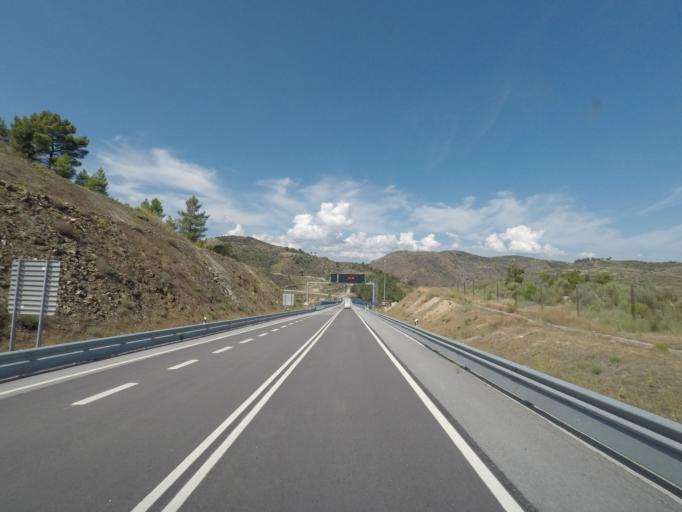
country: PT
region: Braganca
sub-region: Carrazeda de Ansiaes
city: Carrazeda de Anciaes
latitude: 41.3199
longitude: -7.3612
